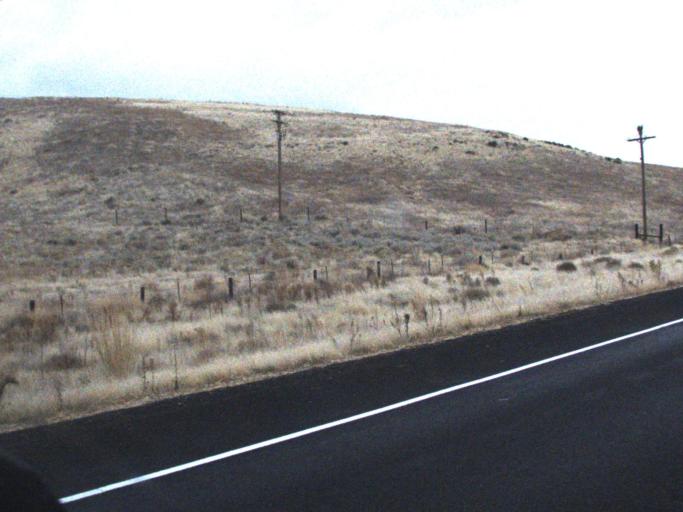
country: US
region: Washington
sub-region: Columbia County
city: Dayton
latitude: 46.7647
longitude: -117.9999
